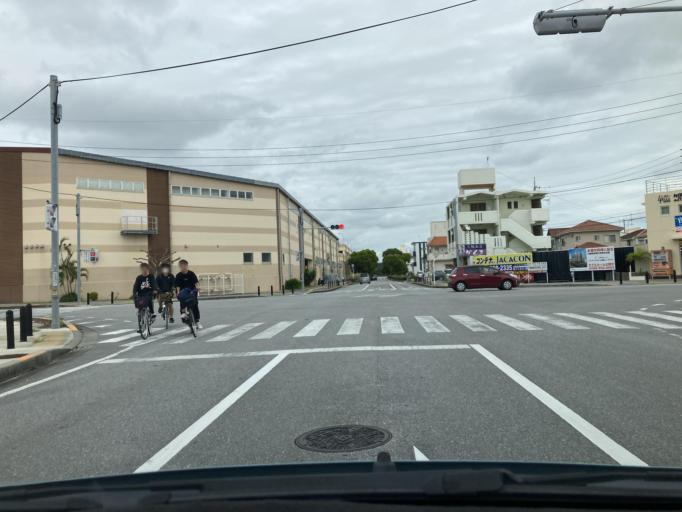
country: JP
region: Okinawa
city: Itoman
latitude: 26.1574
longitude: 127.6593
